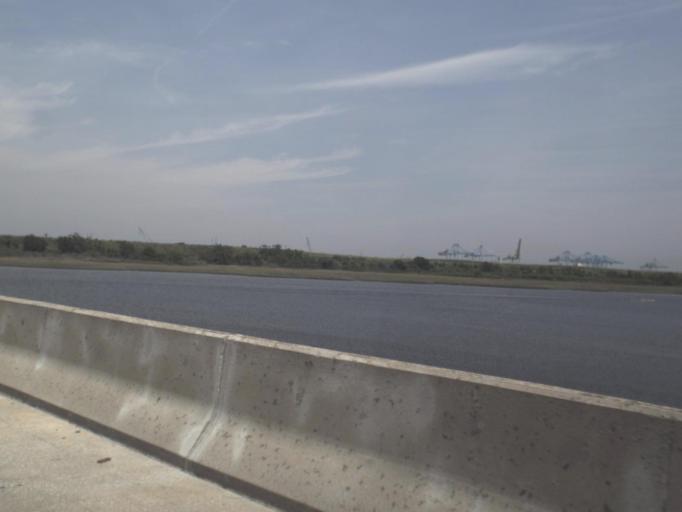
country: US
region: Florida
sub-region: Duval County
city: Jacksonville
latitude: 30.3731
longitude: -81.5520
